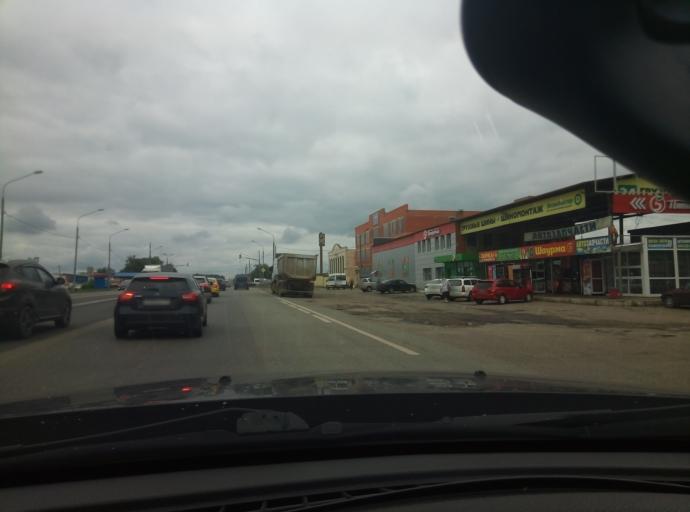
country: RU
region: Kaluga
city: Belousovo
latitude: 55.1076
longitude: 36.6426
